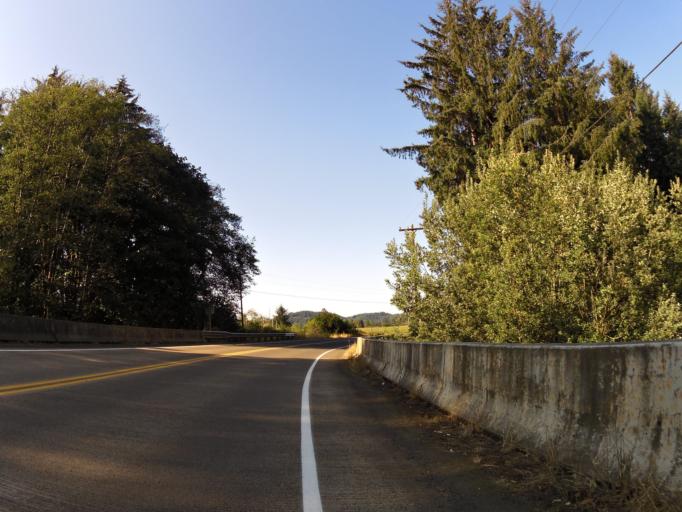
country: US
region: Oregon
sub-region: Tillamook County
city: Tillamook
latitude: 45.3860
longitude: -123.7953
